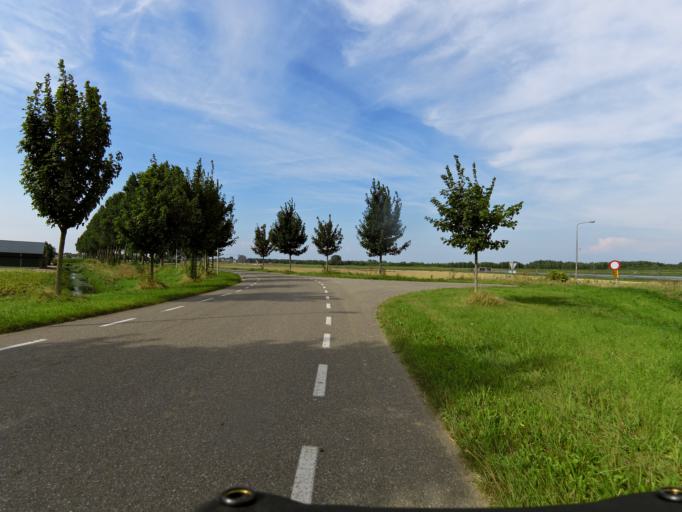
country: NL
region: South Holland
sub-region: Gemeente Zwijndrecht
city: Heerjansdam
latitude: 51.7962
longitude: 4.5850
